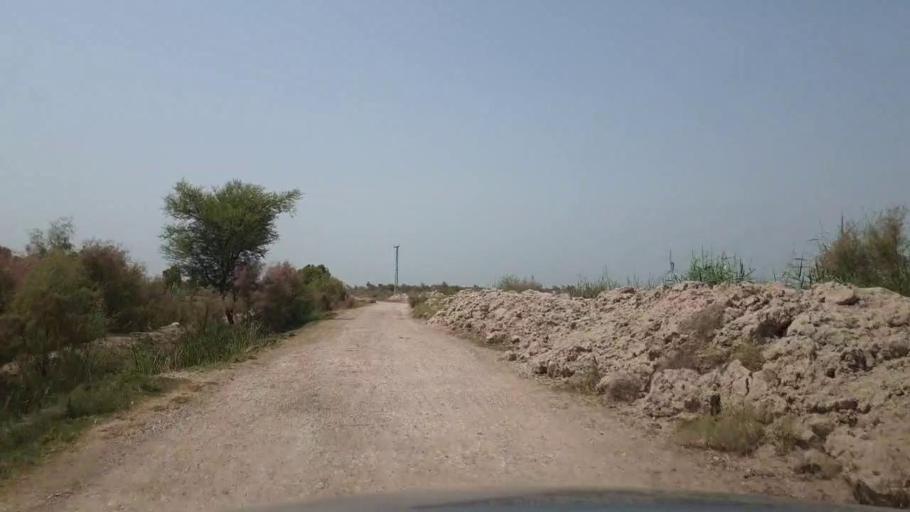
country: PK
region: Sindh
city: Garhi Yasin
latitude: 27.8906
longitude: 68.4558
